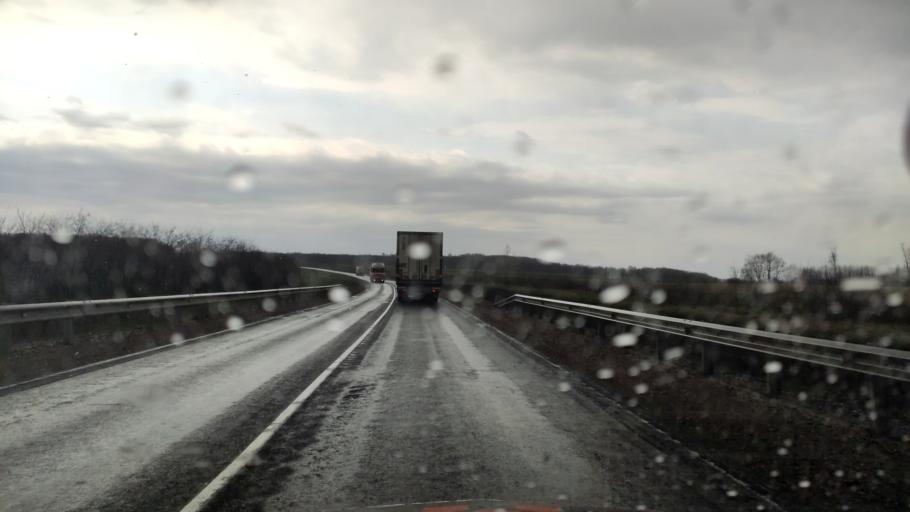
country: RU
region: Voronezj
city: Nizhnedevitsk
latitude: 51.5766
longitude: 38.3162
